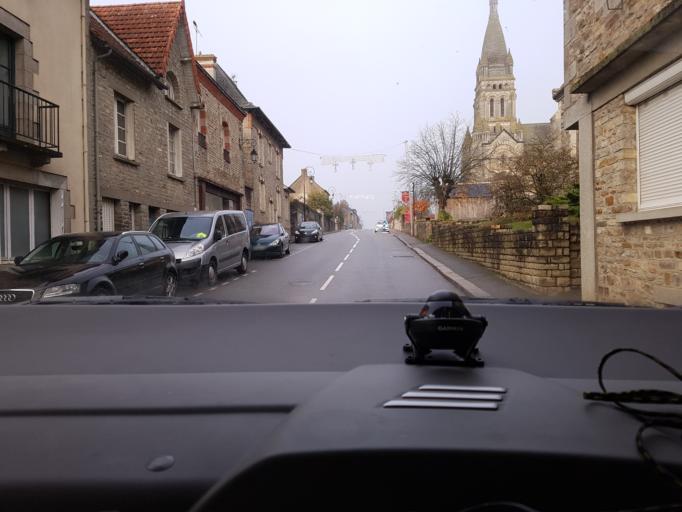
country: FR
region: Brittany
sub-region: Departement d'Ille-et-Vilaine
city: Livre-sur-Changeon
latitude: 48.1770
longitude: -1.3036
